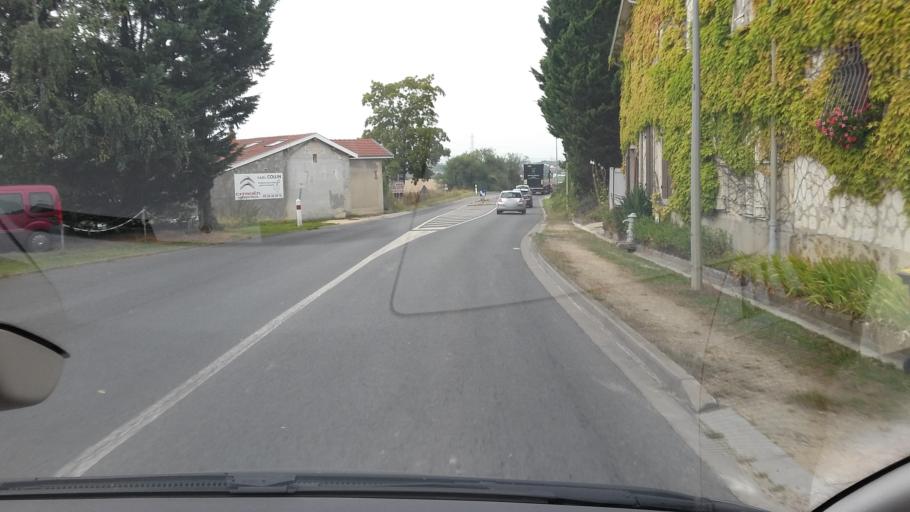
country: FR
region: Champagne-Ardenne
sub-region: Departement de la Marne
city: Cormontreuil
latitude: 49.2026
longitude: 4.0509
